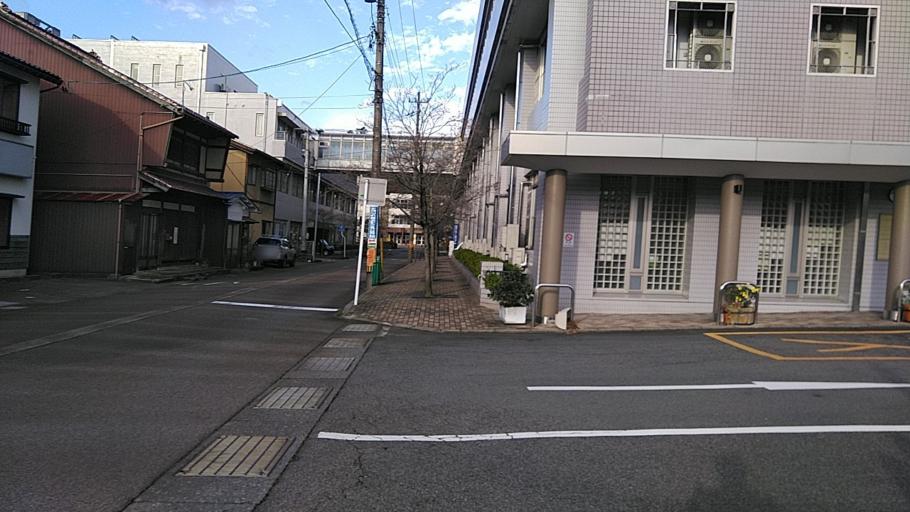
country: JP
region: Fukui
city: Maruoka
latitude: 36.3076
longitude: 136.3102
